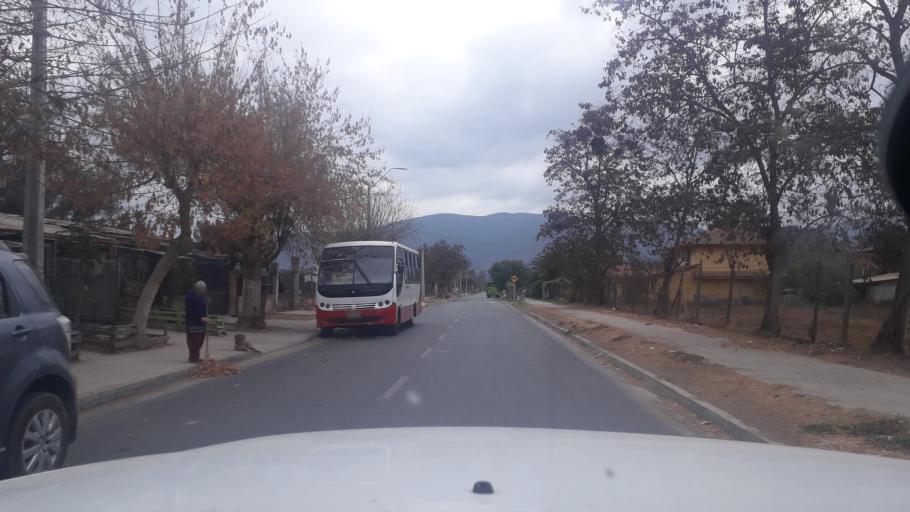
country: CL
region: Valparaiso
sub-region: Provincia de Marga Marga
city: Limache
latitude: -33.0188
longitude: -71.2695
